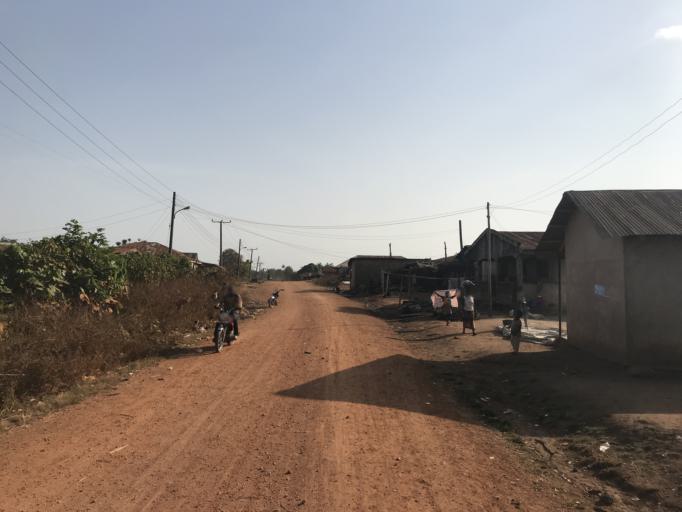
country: NG
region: Osun
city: Awo
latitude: 7.7547
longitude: 4.3170
